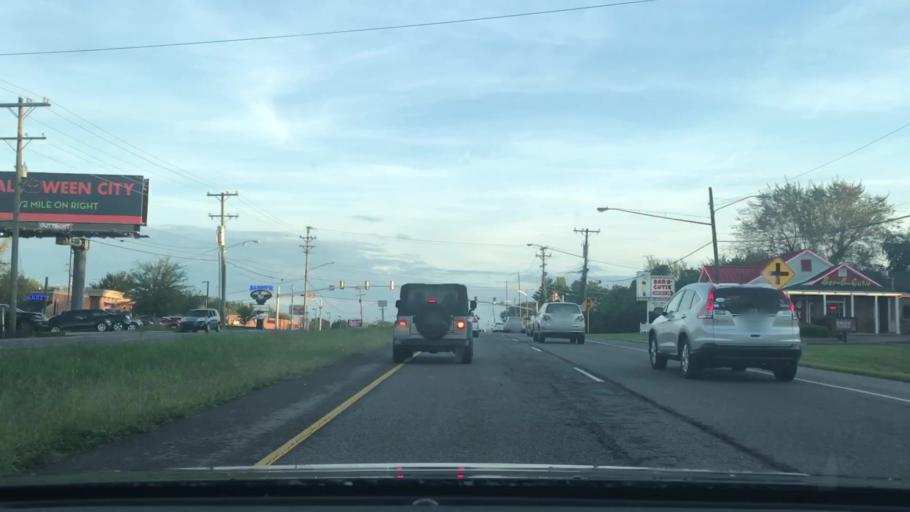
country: US
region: Tennessee
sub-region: Williamson County
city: Brentwood Estates
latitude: 36.0549
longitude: -86.7155
